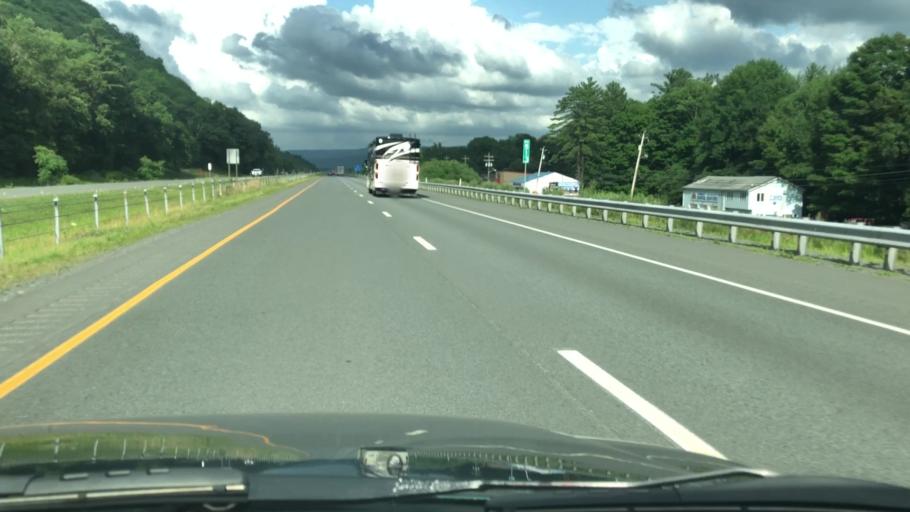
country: US
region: Pennsylvania
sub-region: Pike County
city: Matamoras
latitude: 41.3487
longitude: -74.7493
